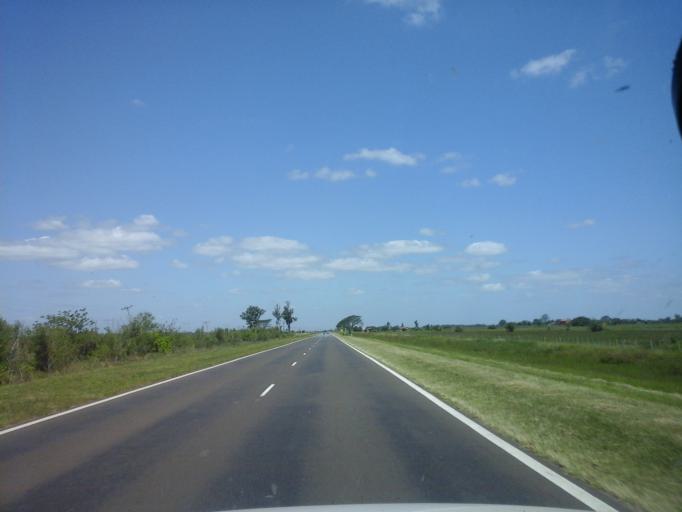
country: PY
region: Neembucu
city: Cerrito
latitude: -27.3537
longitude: -57.8698
